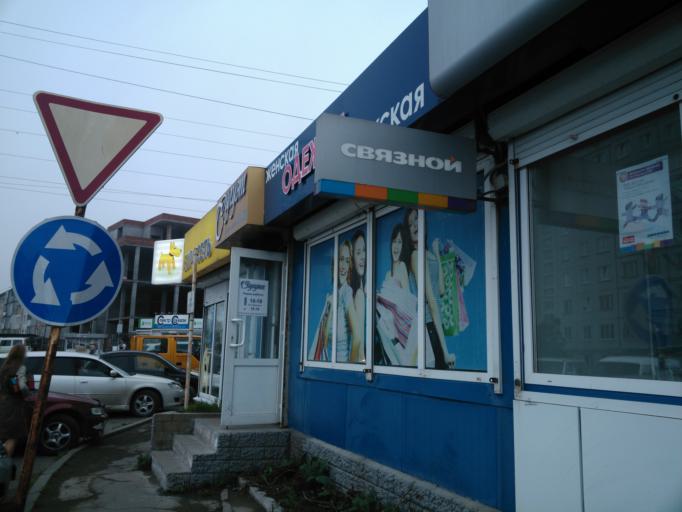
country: RU
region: Primorskiy
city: Vladivostok
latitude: 43.0917
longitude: 131.9712
